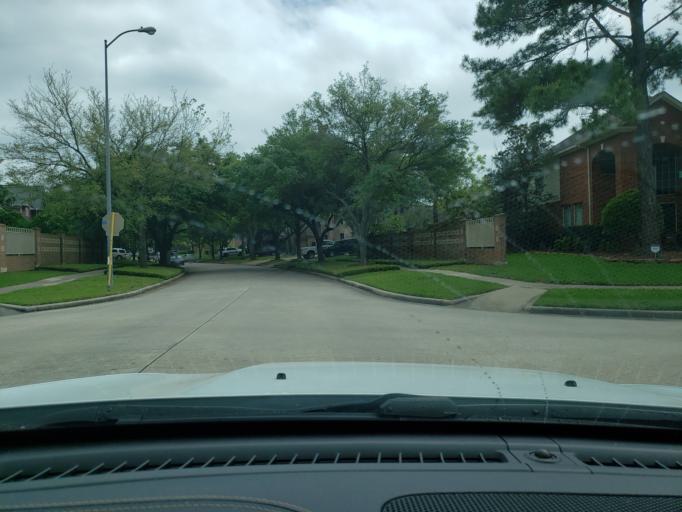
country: US
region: Texas
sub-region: Harris County
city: Jersey Village
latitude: 29.9215
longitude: -95.5653
